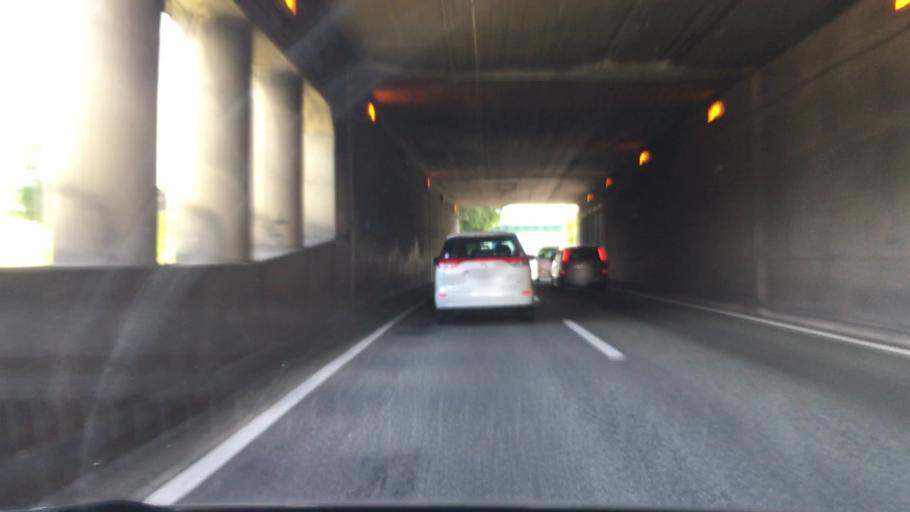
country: JP
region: Fukuoka
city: Onojo
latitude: 33.5323
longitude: 130.4909
